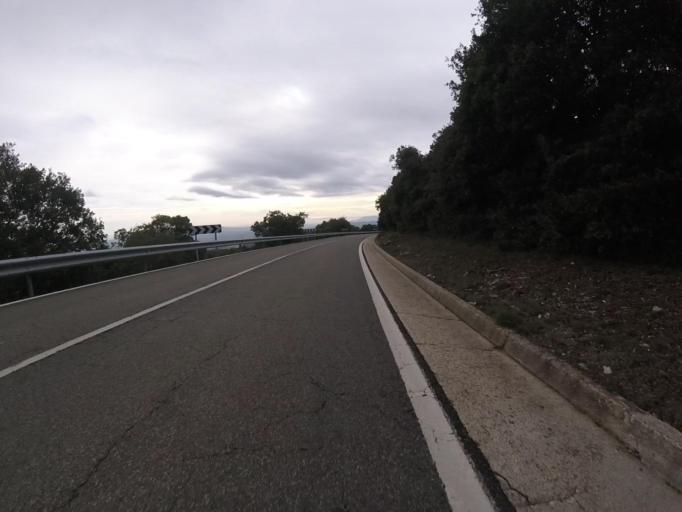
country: ES
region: Navarre
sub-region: Provincia de Navarra
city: Lezaun
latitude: 42.7559
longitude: -2.0114
